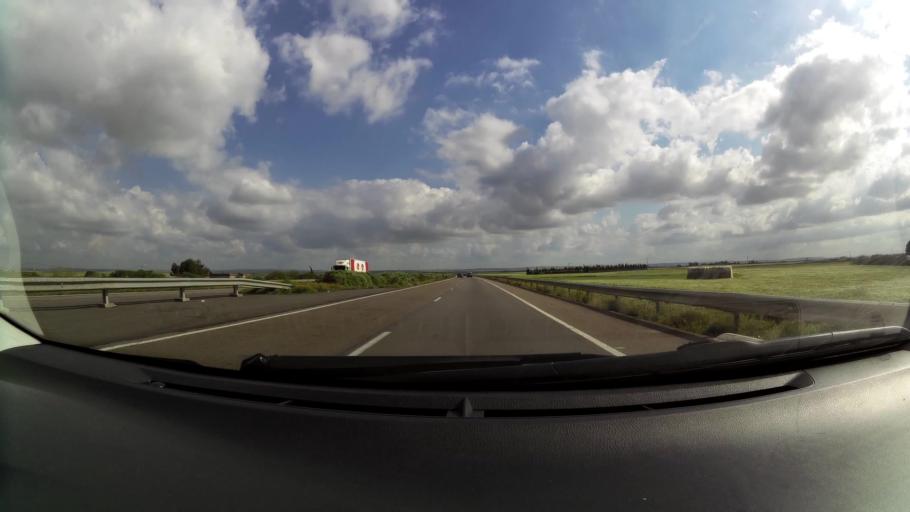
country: MA
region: Chaouia-Ouardigha
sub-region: Settat Province
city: Berrechid
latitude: 33.1935
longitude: -7.5758
